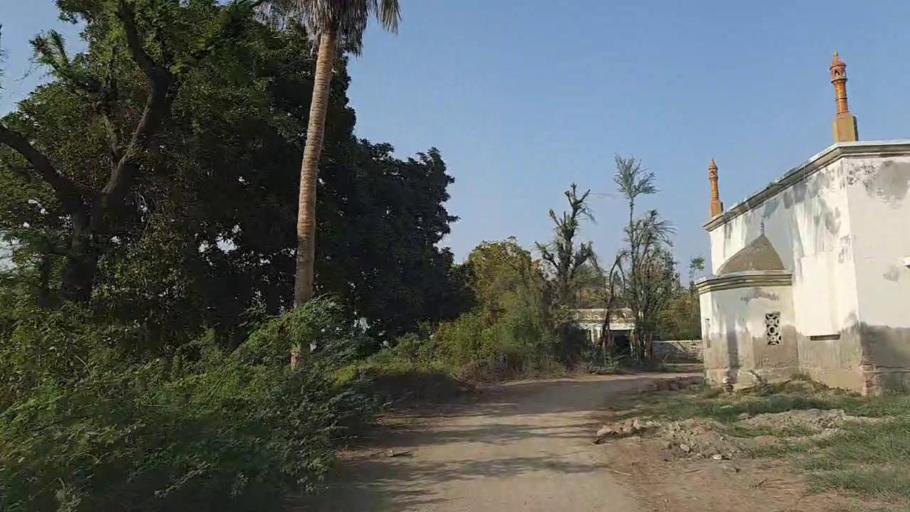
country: PK
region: Sindh
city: Dhoro Naro
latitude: 25.5105
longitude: 69.5344
